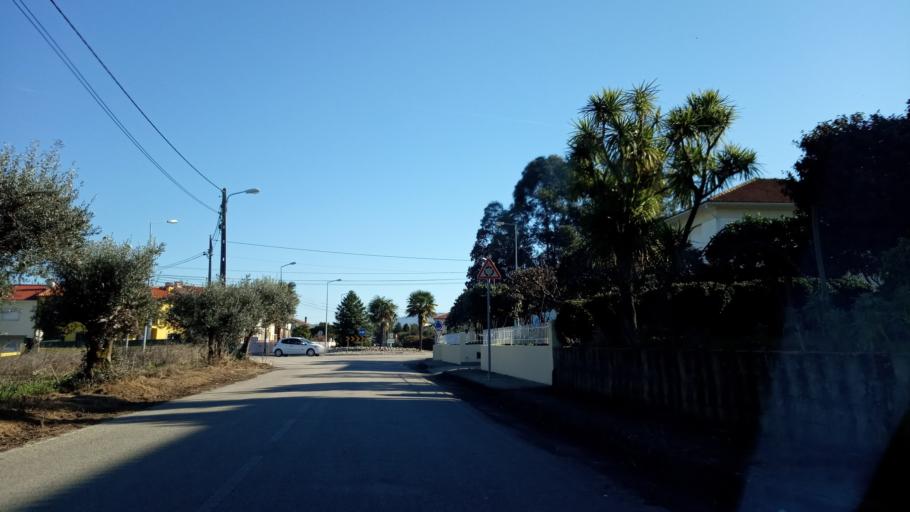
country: PT
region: Aveiro
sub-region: Anadia
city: Anadia
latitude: 40.4258
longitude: -8.4262
